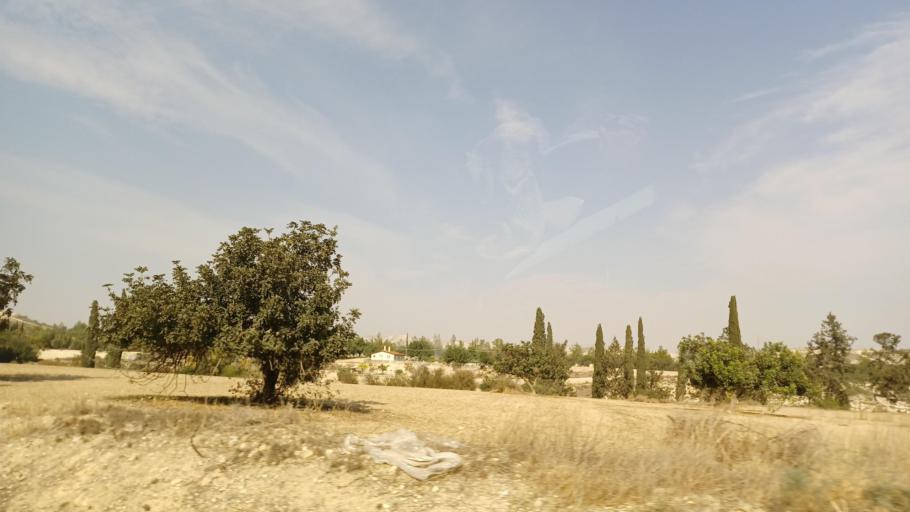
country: CY
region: Larnaka
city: Aradippou
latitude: 34.9639
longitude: 33.5573
